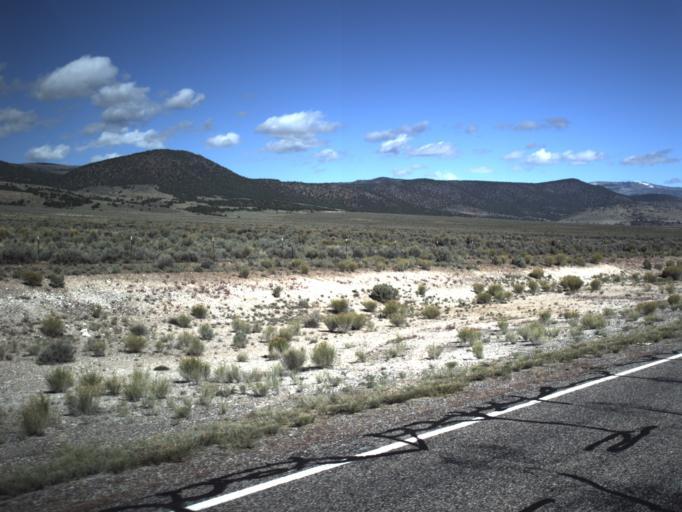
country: US
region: Utah
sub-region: Wayne County
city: Loa
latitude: 38.3968
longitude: -111.9308
